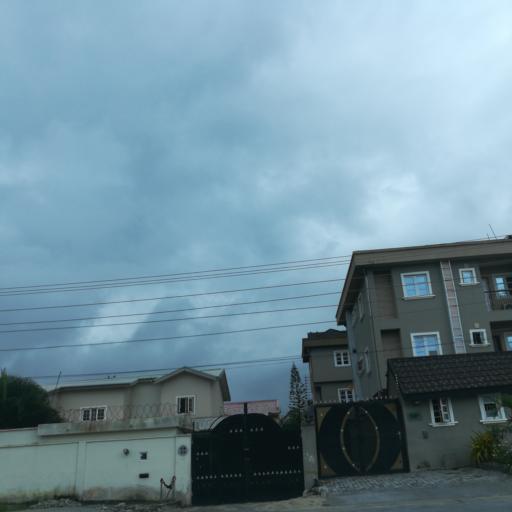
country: NG
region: Lagos
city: Ikoyi
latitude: 6.4371
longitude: 3.4654
